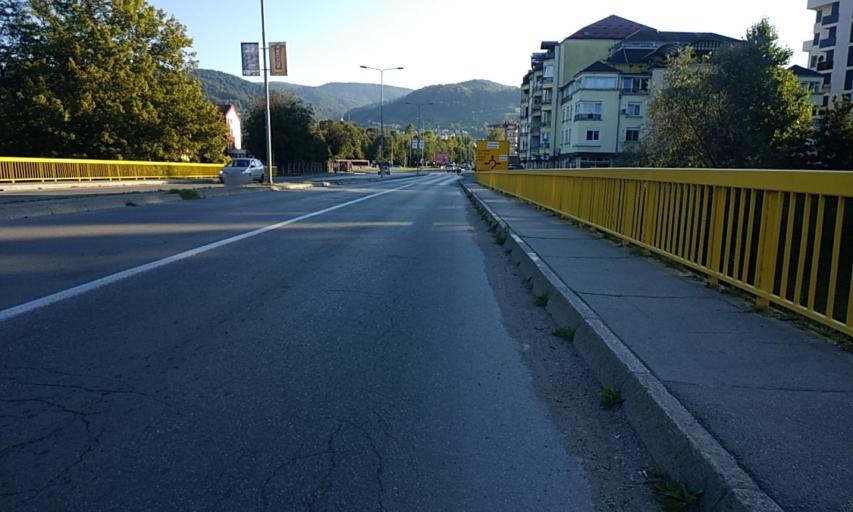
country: BA
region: Republika Srpska
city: Starcevica
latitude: 44.7678
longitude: 17.2097
